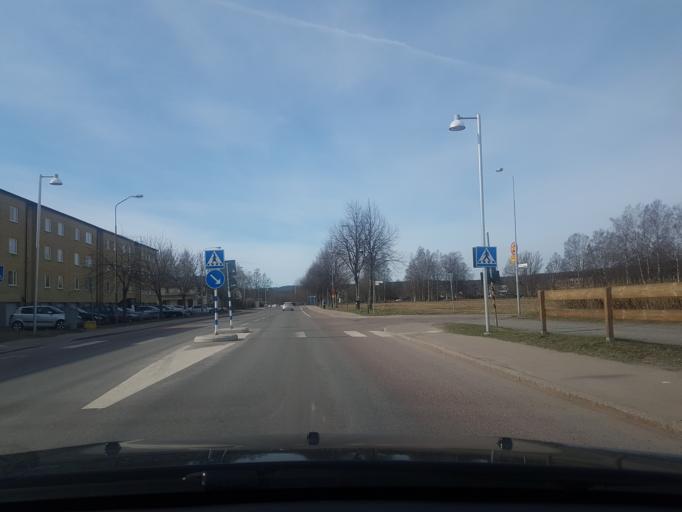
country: SE
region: Dalarna
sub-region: Borlange Kommun
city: Borlaenge
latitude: 60.4892
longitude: 15.4188
